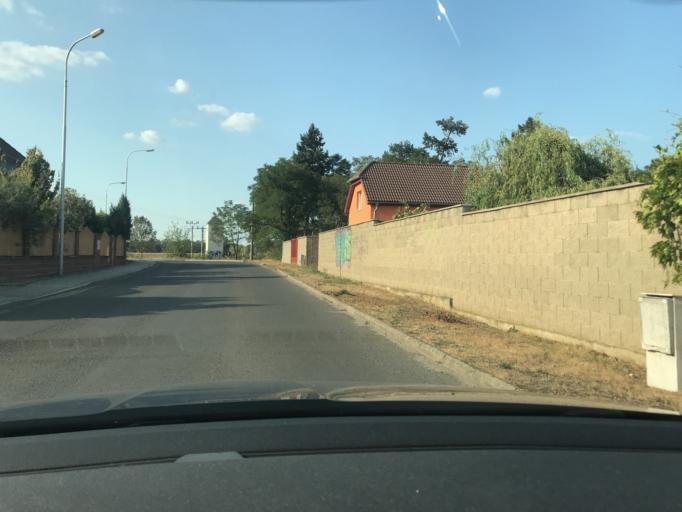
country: CZ
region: Ustecky
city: Postoloprty
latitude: 50.3629
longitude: 13.6915
